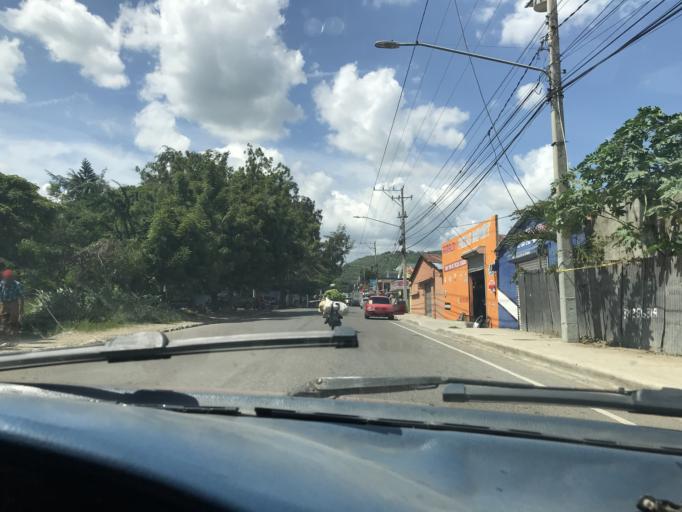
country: DO
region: Santiago
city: Tamboril
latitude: 19.4943
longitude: -70.6538
